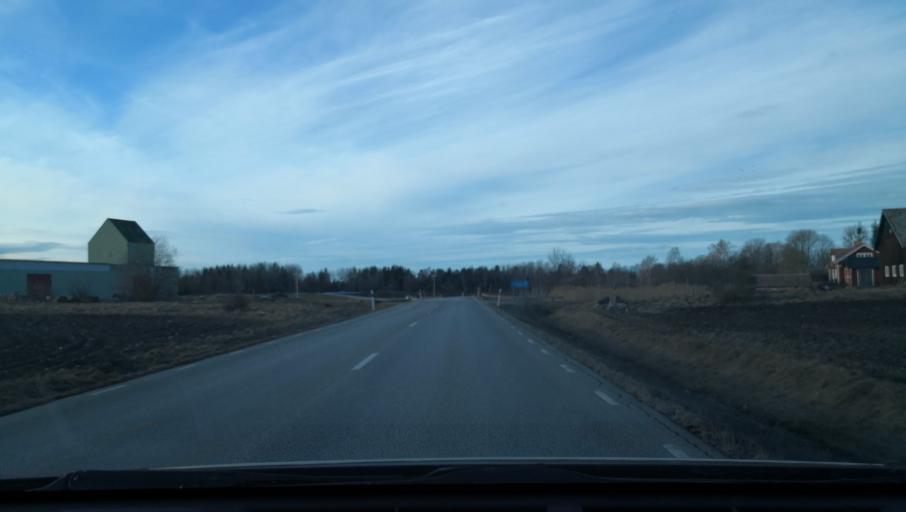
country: SE
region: Uppsala
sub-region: Osthammars Kommun
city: OEsthammar
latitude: 60.3203
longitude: 18.2572
